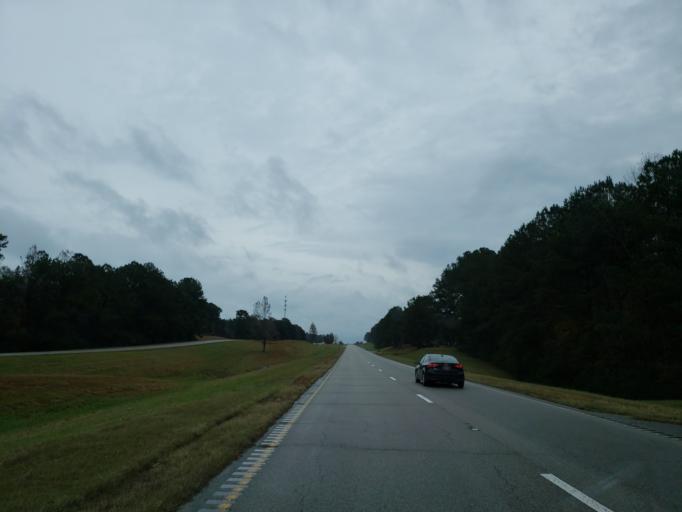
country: US
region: Mississippi
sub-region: Jones County
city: Sharon
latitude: 31.7055
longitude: -88.9316
